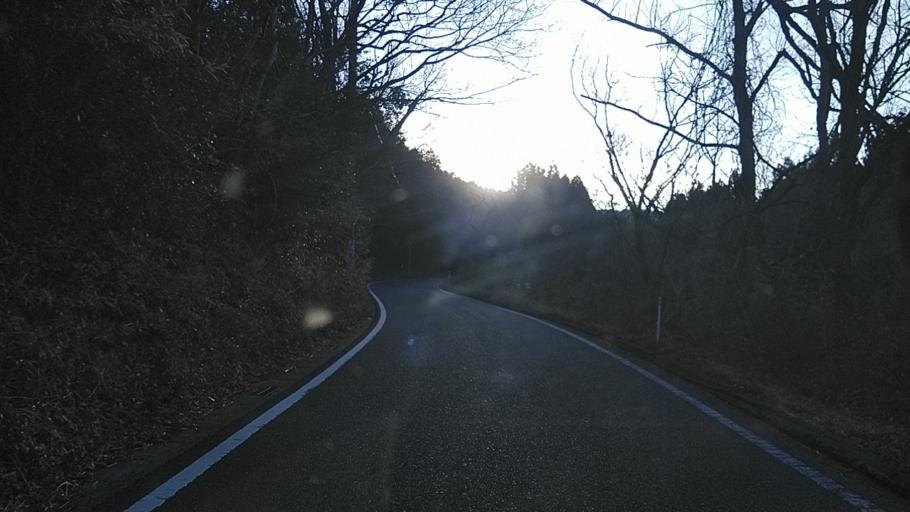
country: JP
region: Chiba
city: Kimitsu
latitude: 35.2603
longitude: 139.9438
